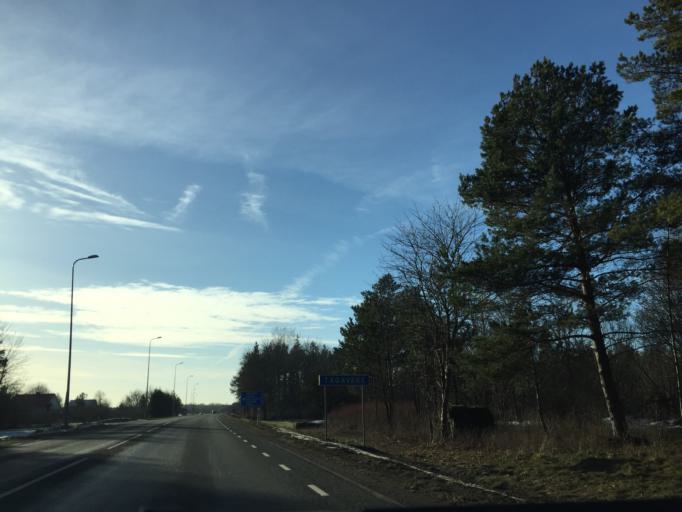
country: EE
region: Saare
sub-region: Orissaare vald
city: Orissaare
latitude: 58.5197
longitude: 22.8945
